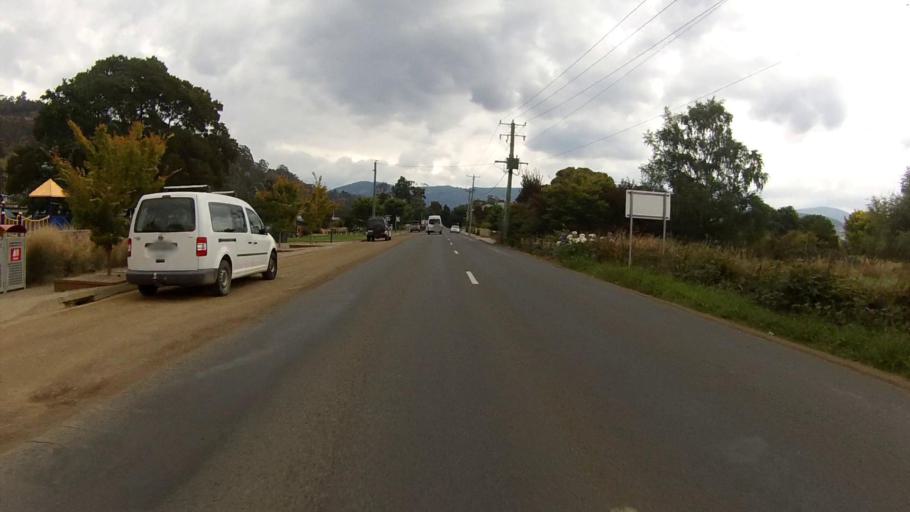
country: AU
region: Tasmania
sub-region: Huon Valley
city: Huonville
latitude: -43.0344
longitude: 147.0494
